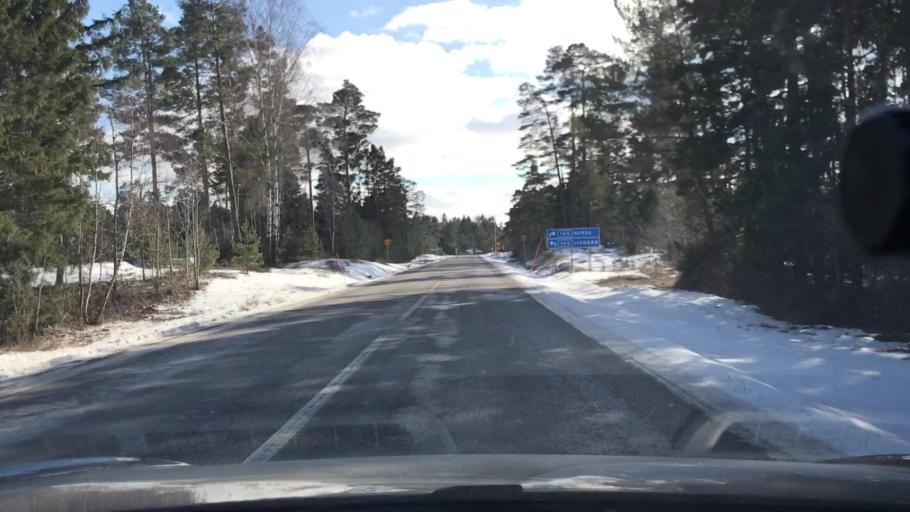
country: SE
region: Gotland
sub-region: Gotland
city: Hemse
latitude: 57.3430
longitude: 18.6930
